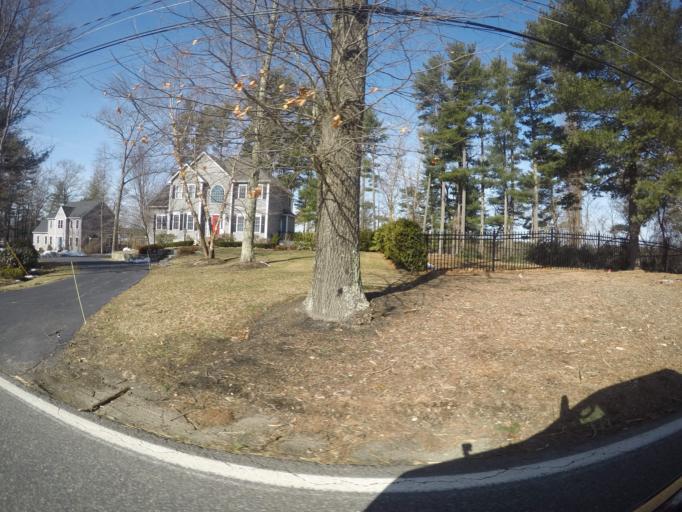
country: US
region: Massachusetts
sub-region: Bristol County
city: Easton
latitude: 41.9967
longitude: -71.1234
